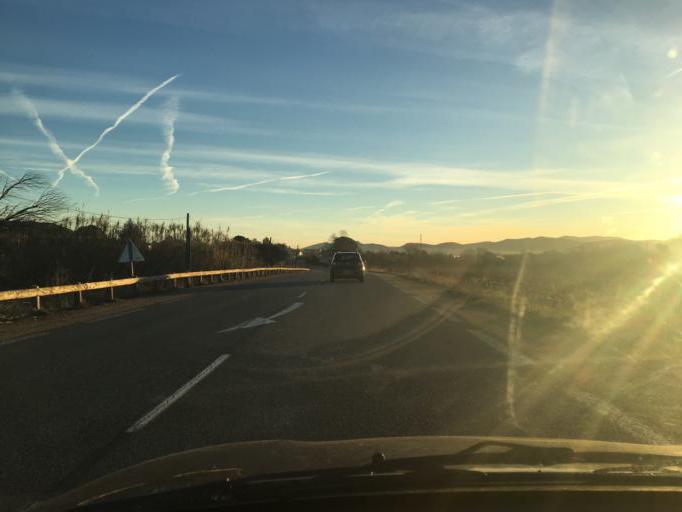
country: FR
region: Provence-Alpes-Cote d'Azur
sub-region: Departement du Var
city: Les Arcs
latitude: 43.4502
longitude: 6.4544
